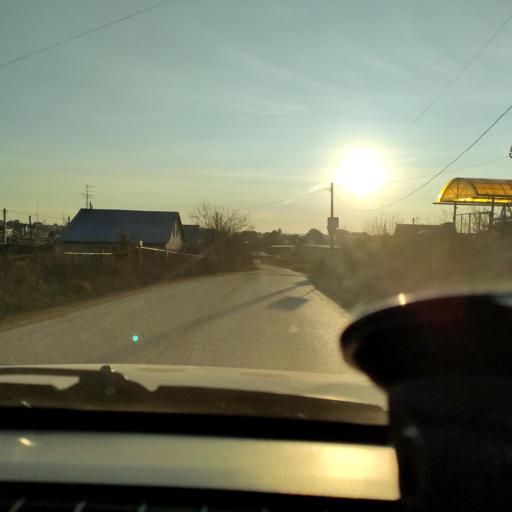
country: RU
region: Perm
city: Ferma
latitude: 57.9483
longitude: 56.3615
